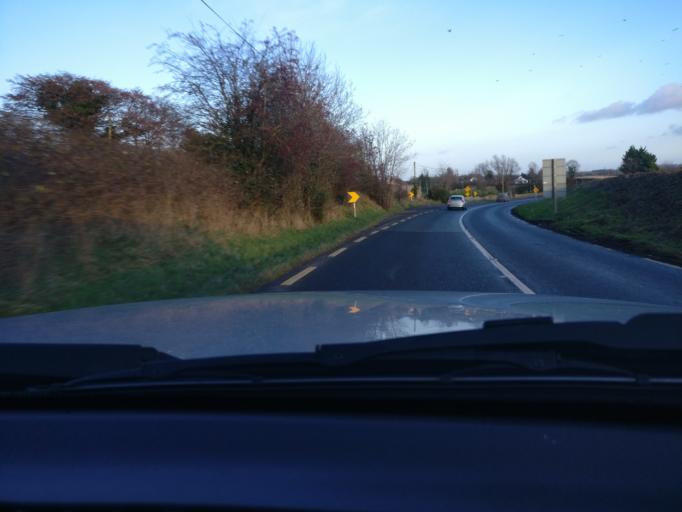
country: IE
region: Leinster
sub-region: Lu
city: Ardee
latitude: 53.8481
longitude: -6.5978
